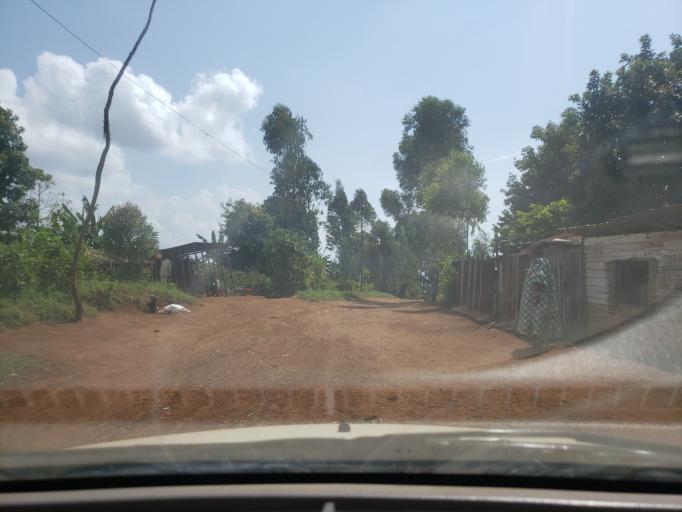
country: CD
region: South Kivu
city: Bukavu
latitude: -2.5054
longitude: 28.8253
